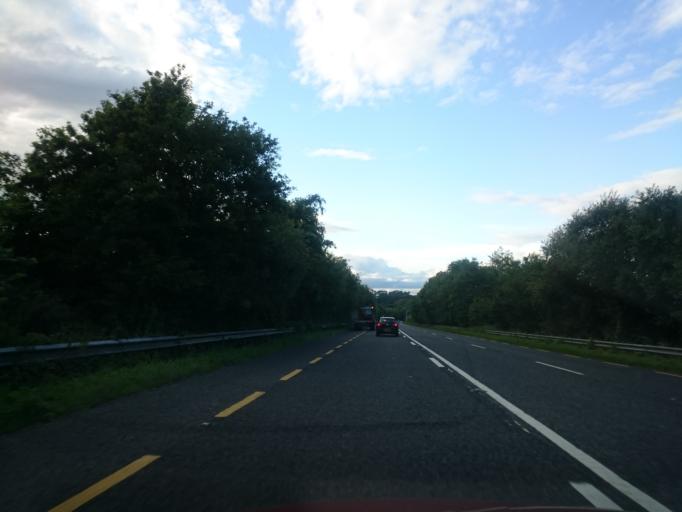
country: IE
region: Leinster
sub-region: Loch Garman
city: Loch Garman
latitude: 52.3441
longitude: -6.5151
